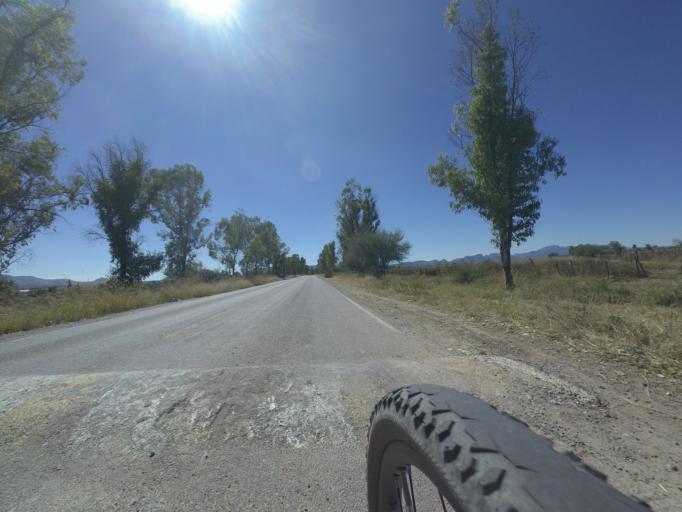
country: MX
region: Aguascalientes
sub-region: Aguascalientes
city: Los Canos
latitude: 21.8818
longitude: -102.4934
